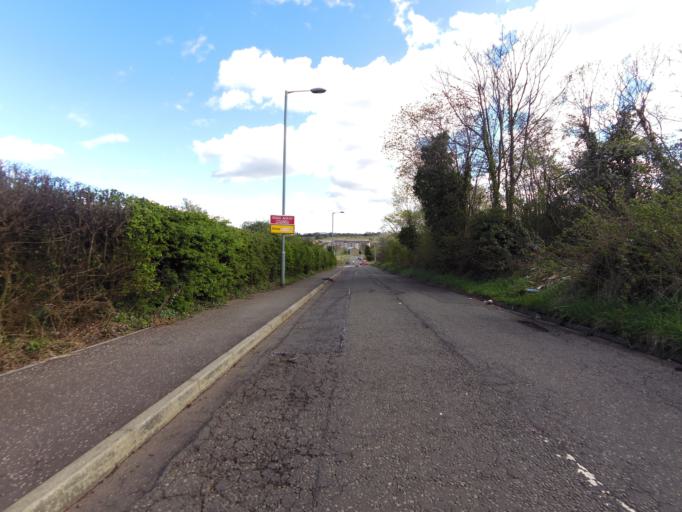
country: GB
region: Scotland
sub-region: West Lothian
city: Seafield
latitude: 55.9283
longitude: -3.1306
